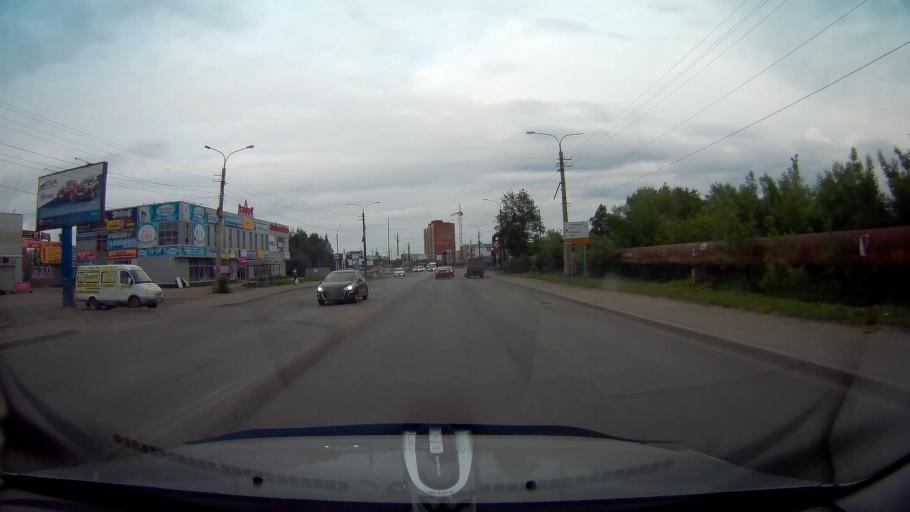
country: RU
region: Arkhangelskaya
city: Arkhangel'sk
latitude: 64.5321
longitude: 40.5956
